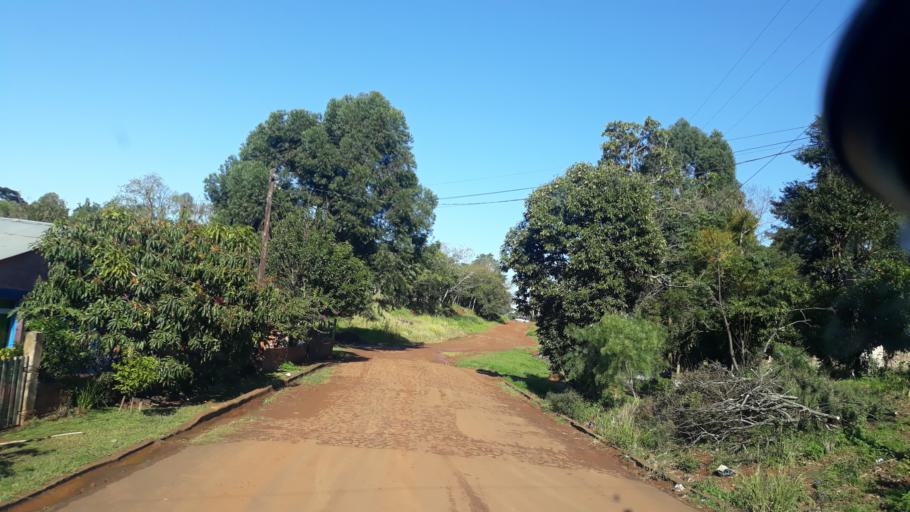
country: AR
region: Misiones
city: Bernardo de Irigoyen
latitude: -26.2632
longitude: -53.6576
